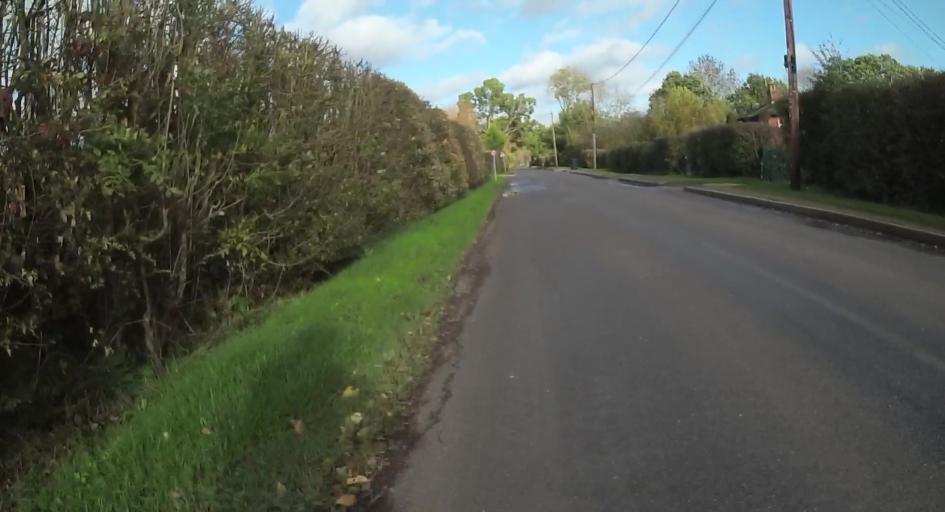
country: GB
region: England
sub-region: West Berkshire
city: Stratfield Mortimer
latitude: 51.3511
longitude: -1.0184
